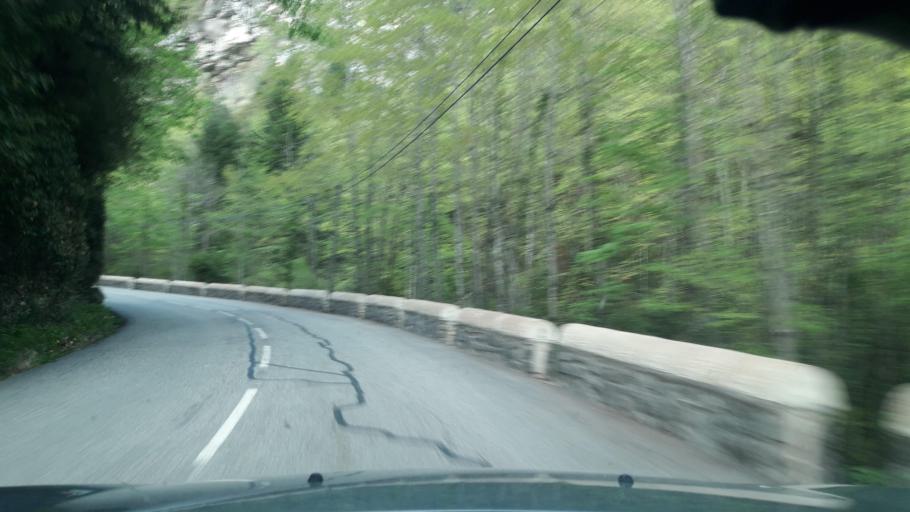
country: FR
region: Rhone-Alpes
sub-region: Departement de la Drome
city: Die
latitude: 44.6740
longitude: 5.5614
